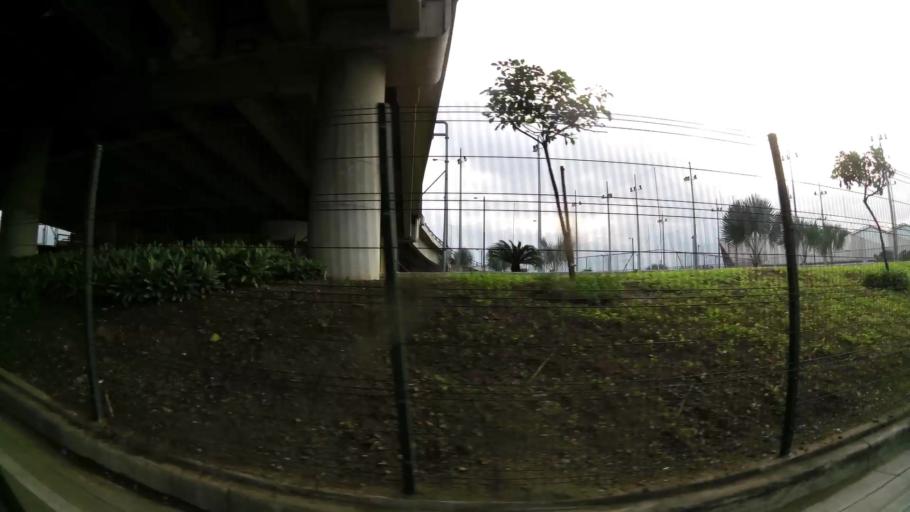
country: EC
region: Guayas
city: Eloy Alfaro
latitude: -2.1402
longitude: -79.8823
